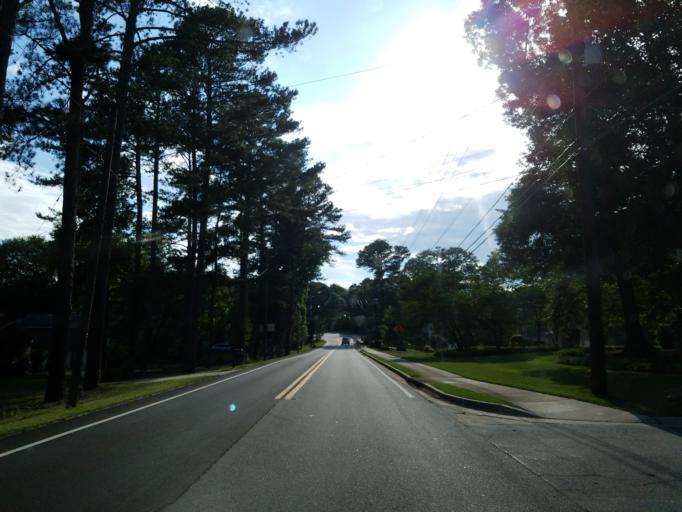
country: US
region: Georgia
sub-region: Cobb County
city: Marietta
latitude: 33.9852
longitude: -84.4568
